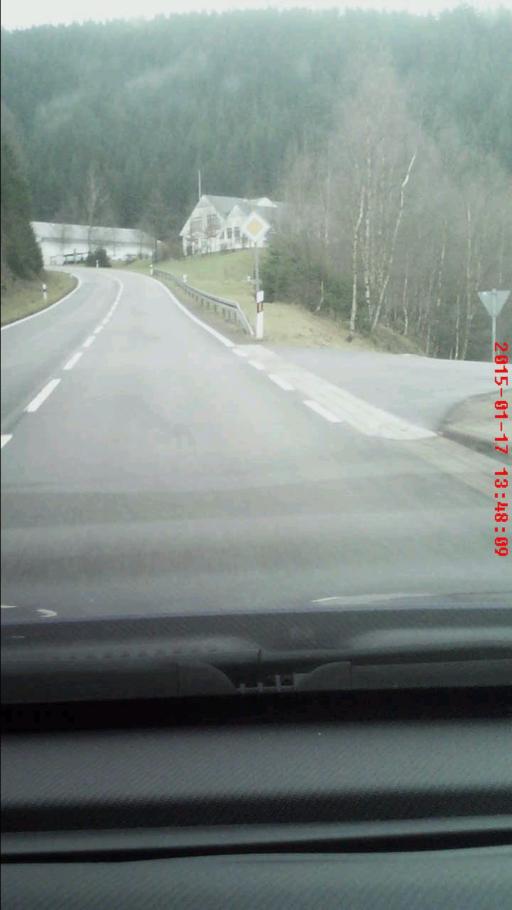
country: DE
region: Thuringia
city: Goldisthal
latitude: 50.5197
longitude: 11.0082
